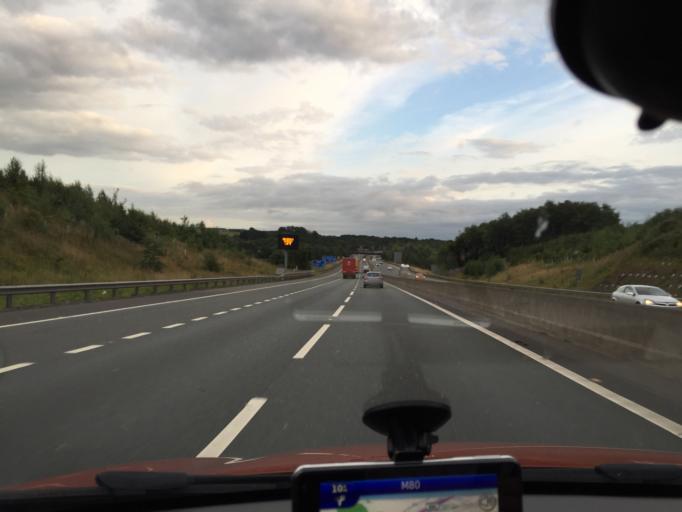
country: GB
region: Scotland
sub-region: Falkirk
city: Dunipace
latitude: 55.9899
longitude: -3.9441
